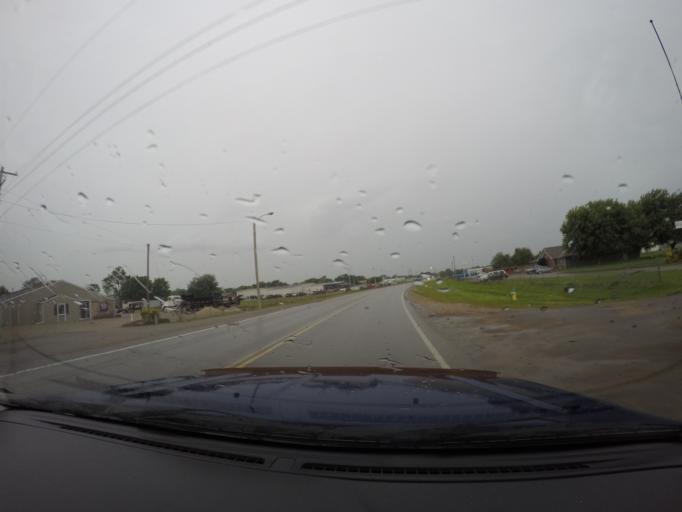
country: US
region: Kansas
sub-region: Cloud County
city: Concordia
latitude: 39.5717
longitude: -97.6380
